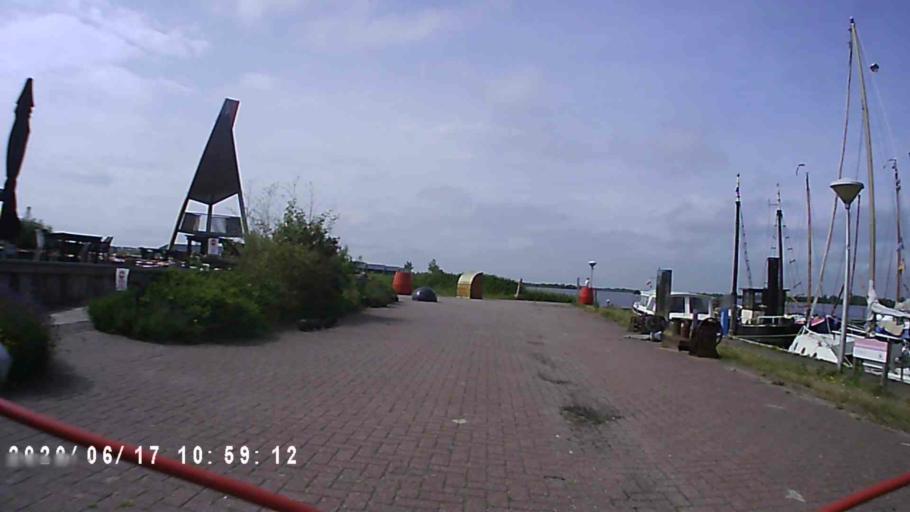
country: NL
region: Friesland
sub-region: Gemeente Dongeradeel
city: Anjum
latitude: 53.4040
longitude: 6.2105
